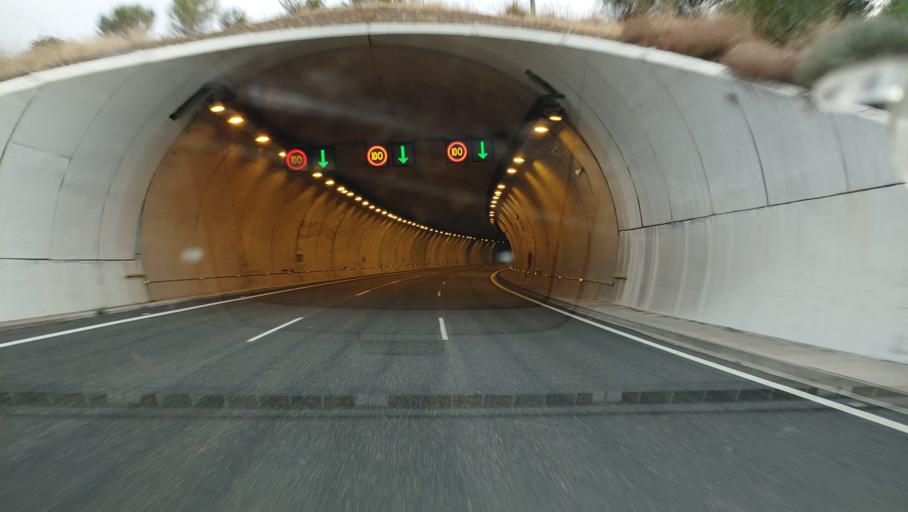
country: ES
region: Andalusia
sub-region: Provincia de Jaen
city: Santa Elena
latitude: 38.3814
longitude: -3.5073
